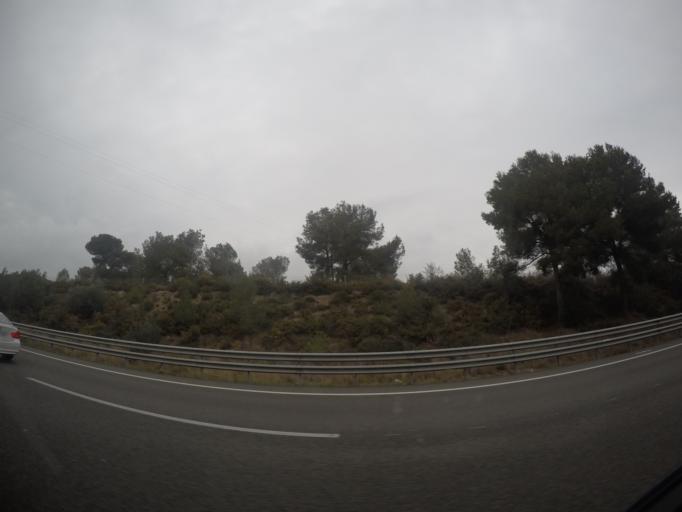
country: ES
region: Catalonia
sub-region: Provincia de Tarragona
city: Sant Jaume dels Domenys
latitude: 41.2881
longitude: 1.5883
